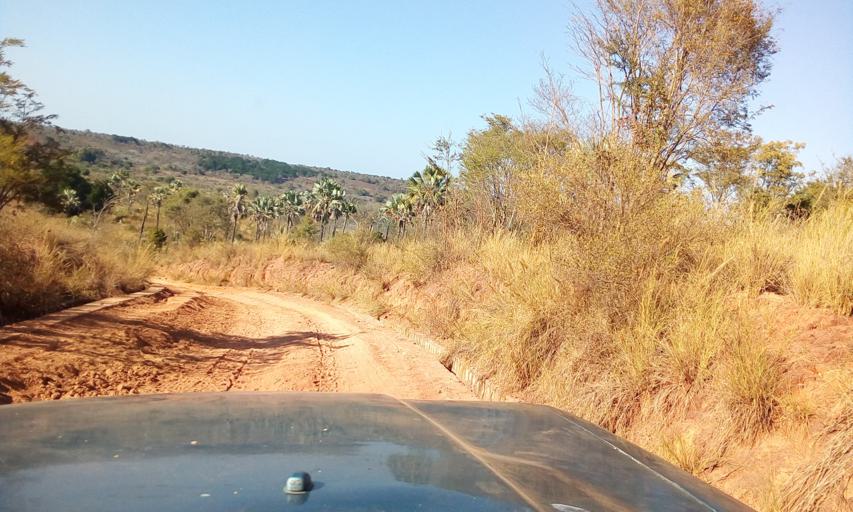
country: MG
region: Melaky
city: Mahabe
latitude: -16.2090
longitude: 45.3532
